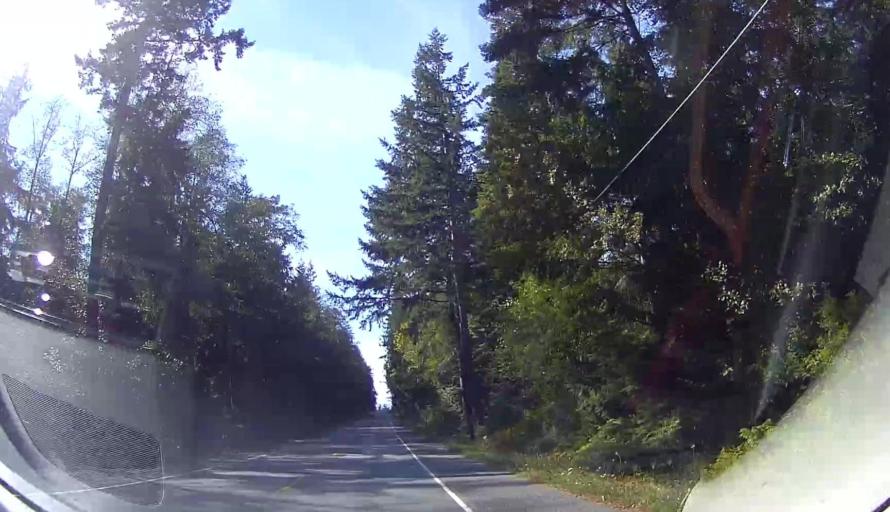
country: US
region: Washington
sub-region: Island County
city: Camano
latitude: 48.2256
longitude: -122.5120
